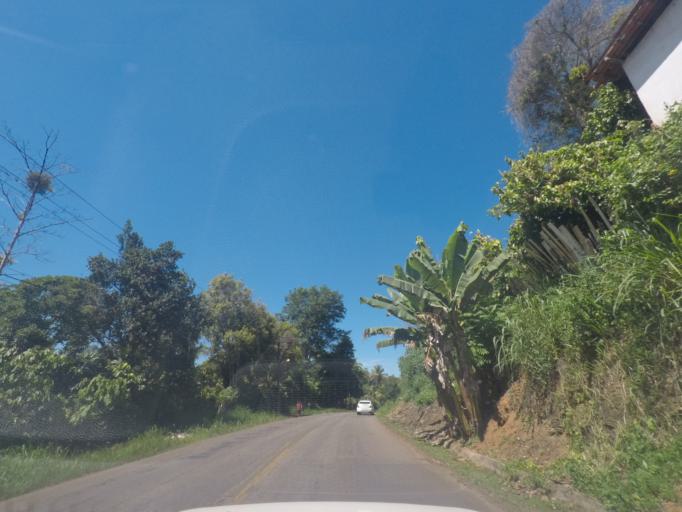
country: BR
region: Bahia
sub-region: Taperoa
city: Taperoa
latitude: -13.4963
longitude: -39.0963
